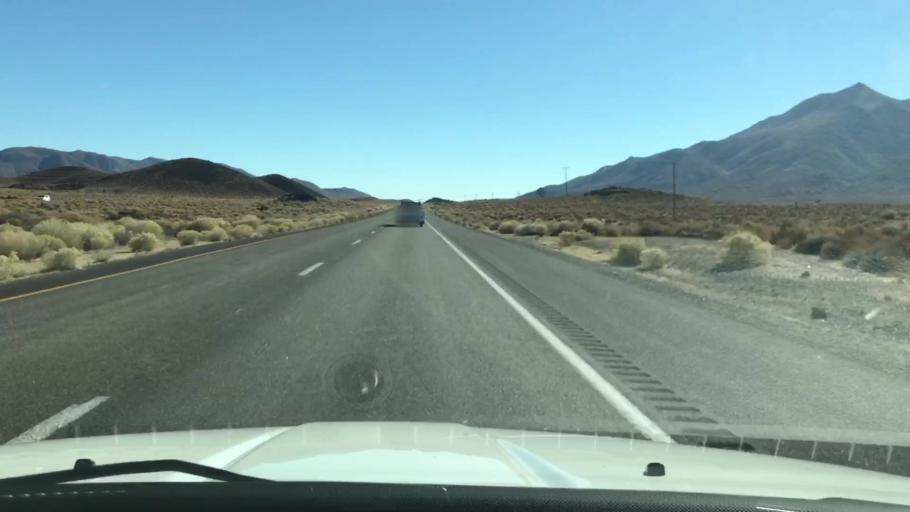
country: US
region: California
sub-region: Kern County
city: Inyokern
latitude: 35.9928
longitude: -117.9306
